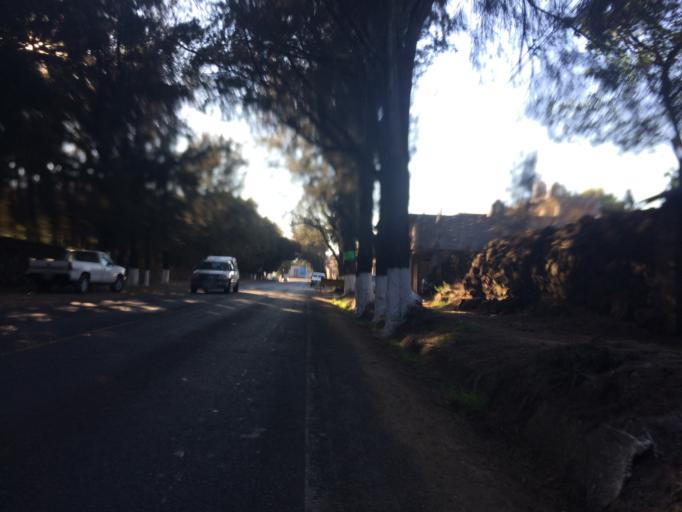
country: MX
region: Michoacan
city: Patzcuaro
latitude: 19.5061
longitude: -101.6074
